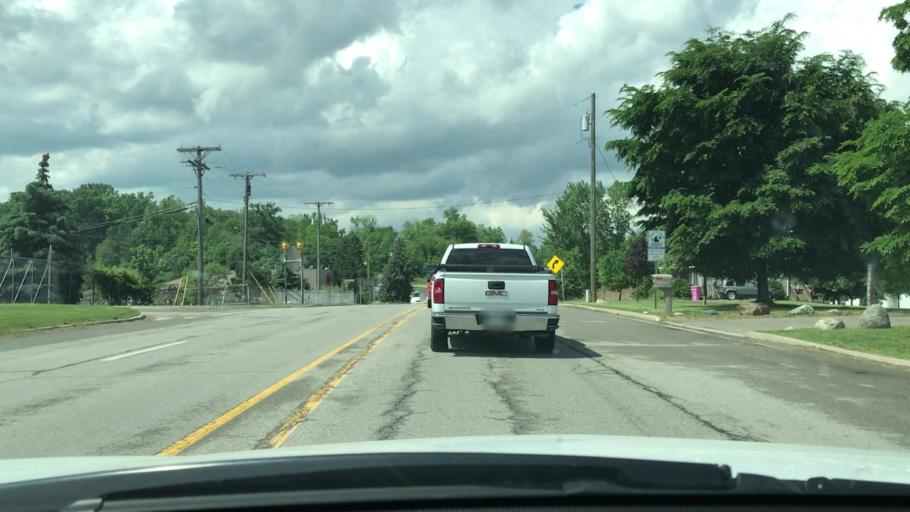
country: US
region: Michigan
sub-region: Oakland County
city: Auburn Hills
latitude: 42.7090
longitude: -83.2855
